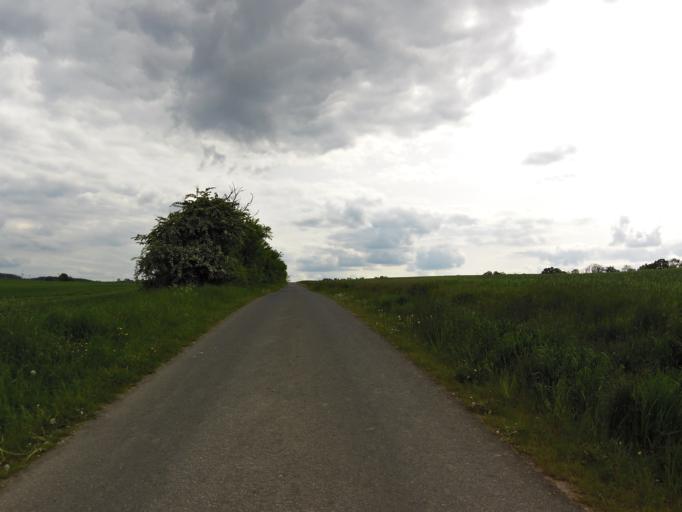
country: DE
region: Thuringia
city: Creuzburg
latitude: 51.0308
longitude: 10.2405
